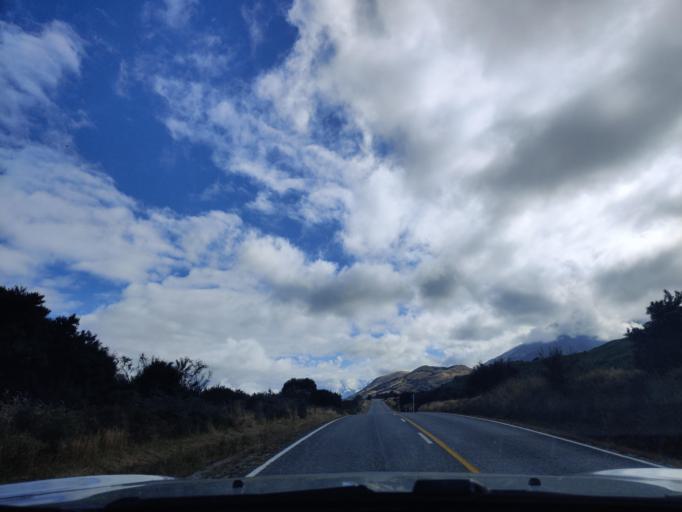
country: NZ
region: Otago
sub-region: Queenstown-Lakes District
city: Queenstown
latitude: -44.8779
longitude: 168.3998
